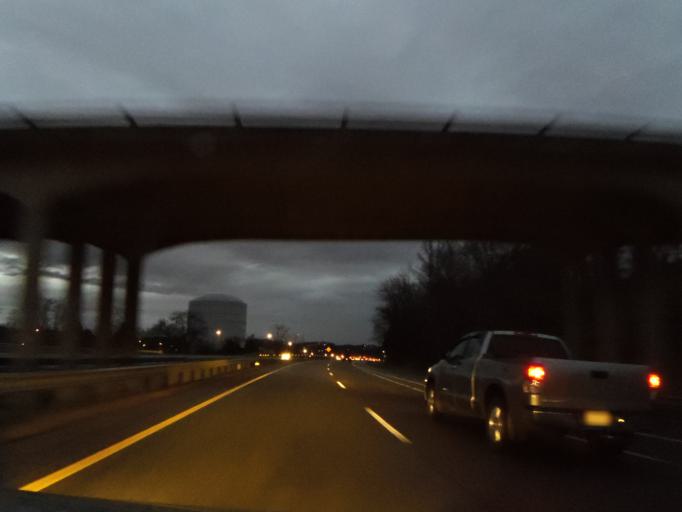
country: US
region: Tennessee
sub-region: Washington County
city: Gray
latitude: 36.4388
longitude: -82.5233
